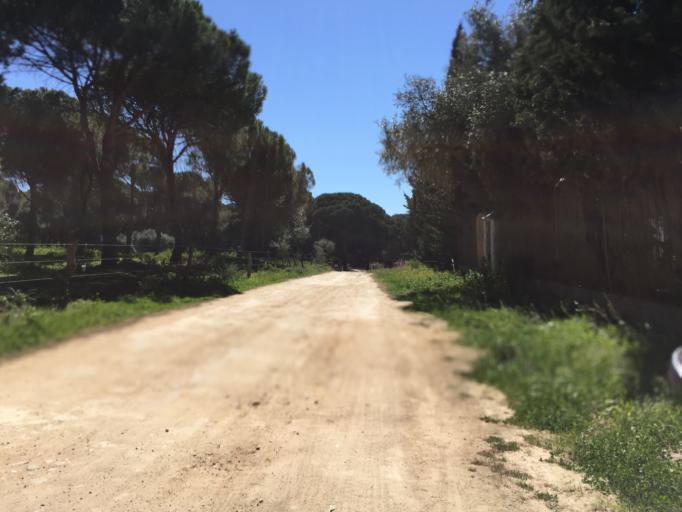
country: ES
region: Andalusia
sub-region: Provincia de Cadiz
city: Vejer de la Frontera
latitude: 36.2062
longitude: -5.9760
